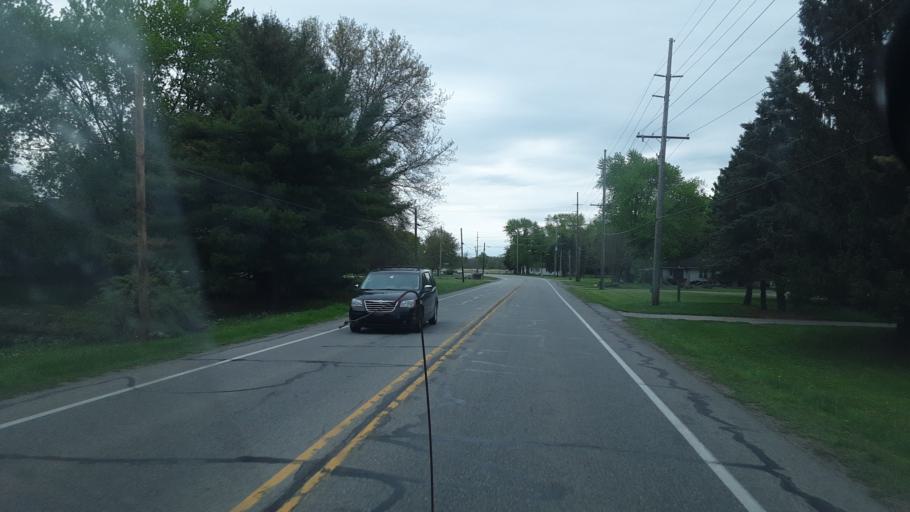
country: US
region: Indiana
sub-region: Elkhart County
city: Goshen
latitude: 41.6096
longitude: -85.8317
